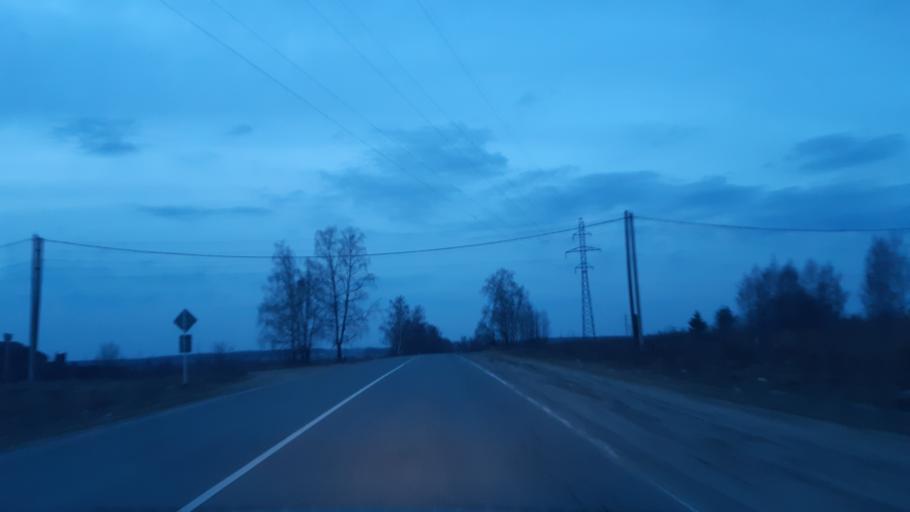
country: RU
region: Vladimir
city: Luknovo
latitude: 56.1994
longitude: 42.0338
